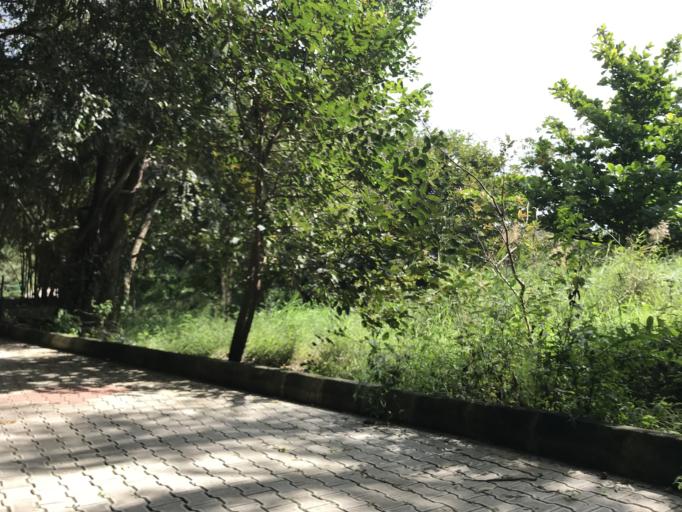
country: IN
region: Karnataka
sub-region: Mandya
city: Shrirangapattana
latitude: 12.4232
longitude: 76.6521
